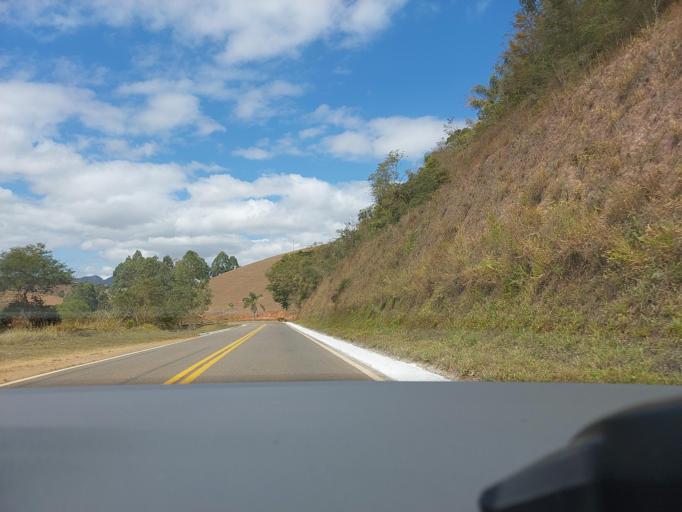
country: BR
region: Minas Gerais
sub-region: Visconde Do Rio Branco
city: Visconde do Rio Branco
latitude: -20.9157
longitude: -42.6401
